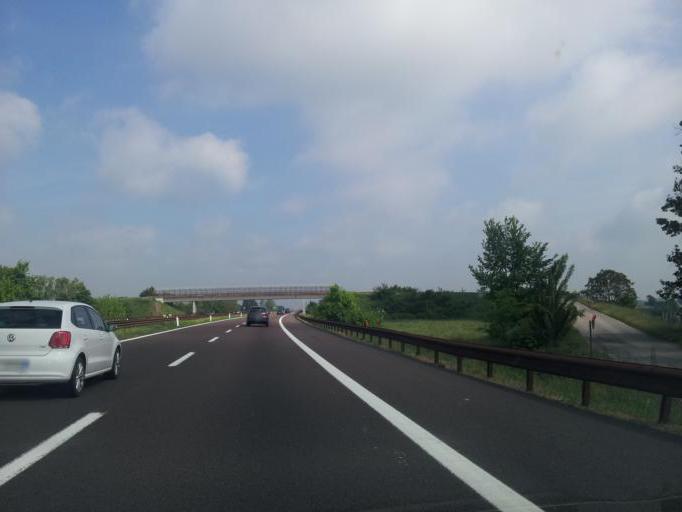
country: IT
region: Lombardy
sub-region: Provincia di Mantova
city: Pegognaga
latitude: 44.9665
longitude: 10.8585
